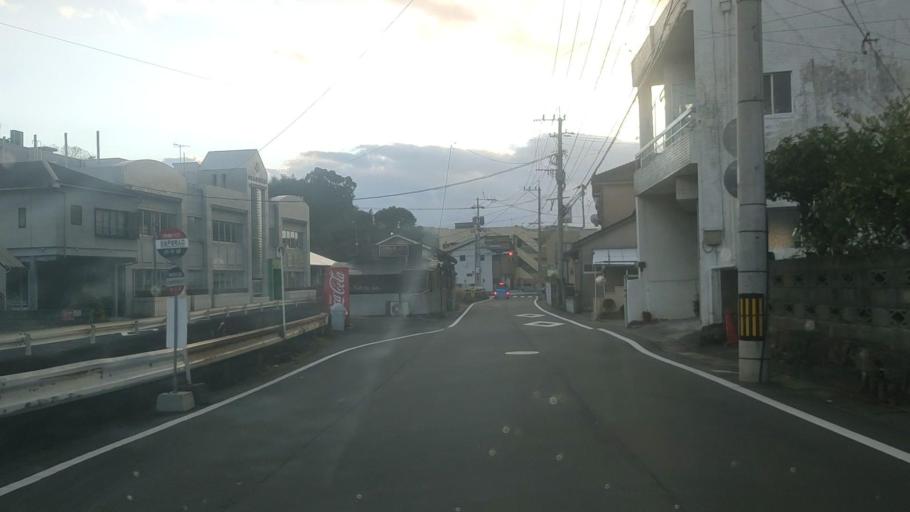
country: JP
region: Kagoshima
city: Kagoshima-shi
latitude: 31.6188
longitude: 130.5358
